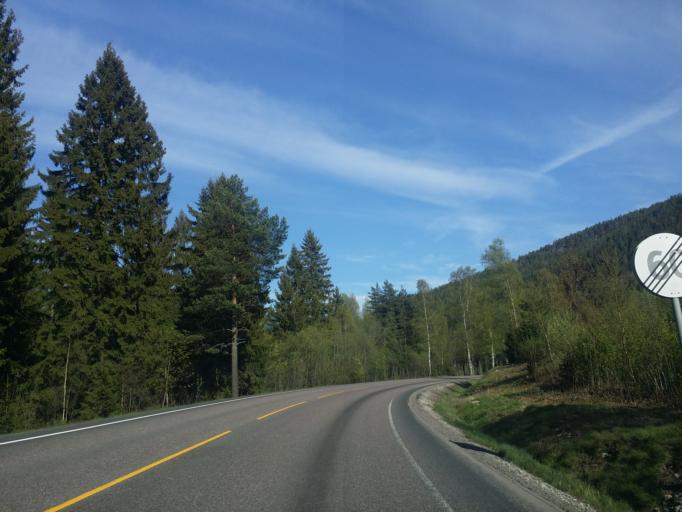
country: NO
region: Telemark
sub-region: Hjartdal
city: Sauland
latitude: 59.6105
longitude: 8.9682
